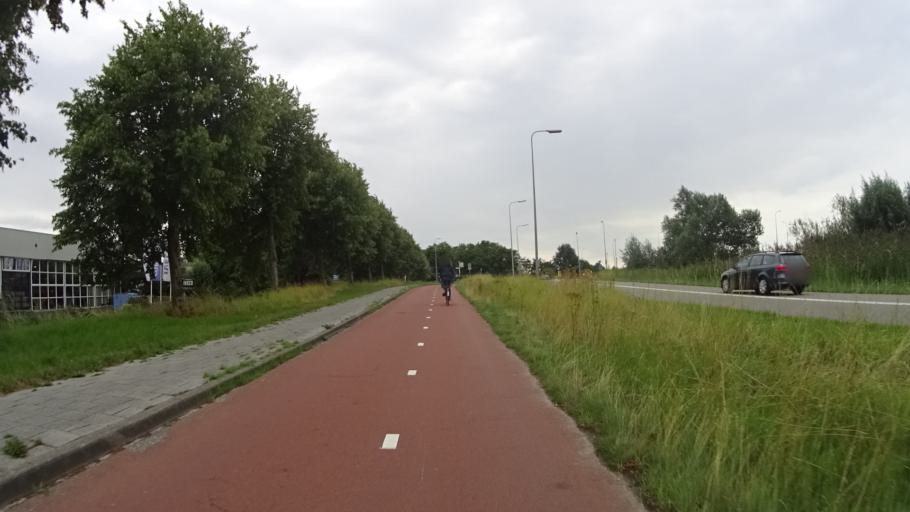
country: NL
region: Groningen
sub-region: Gemeente Groningen
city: Oosterpark
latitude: 53.2271
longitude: 6.5939
